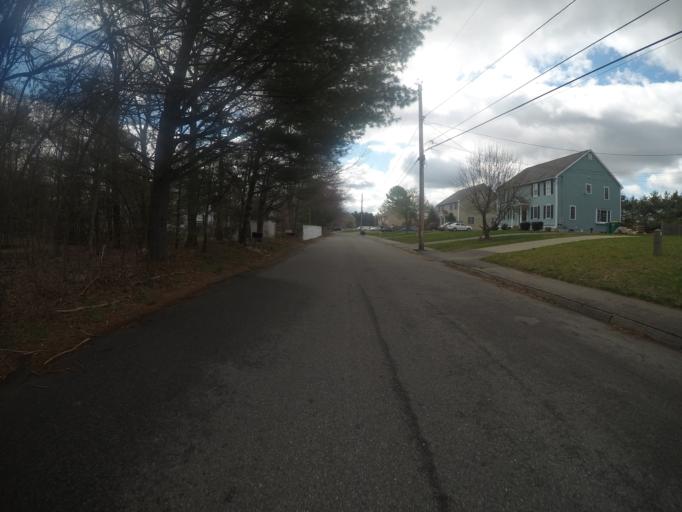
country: US
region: Massachusetts
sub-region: Bristol County
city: Easton
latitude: 42.0279
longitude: -71.1563
